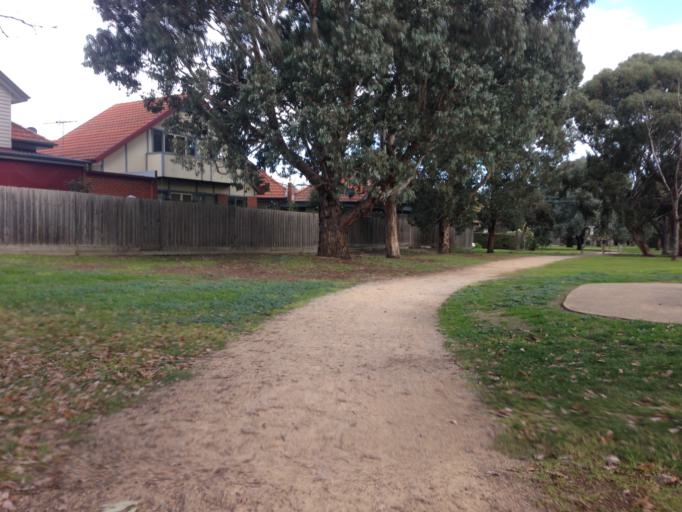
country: AU
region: Victoria
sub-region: Banyule
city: Bellfield
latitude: -37.7587
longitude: 145.0413
